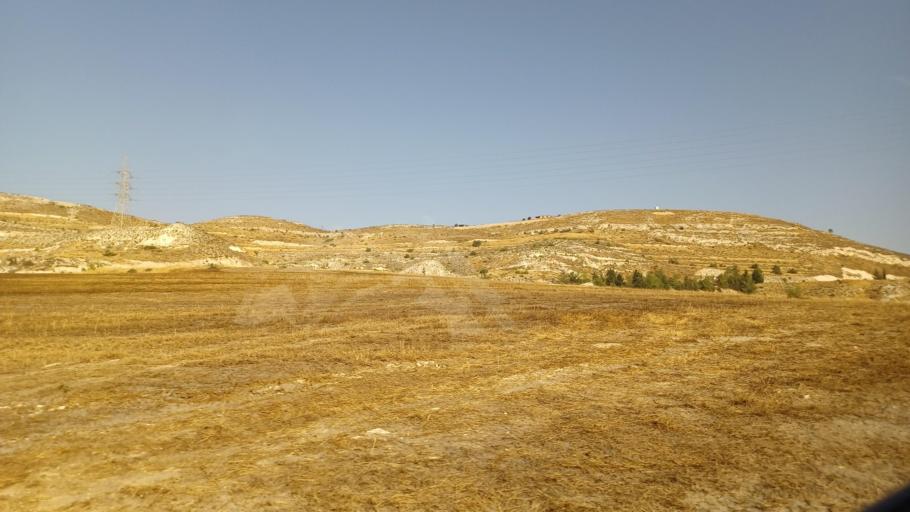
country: CY
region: Larnaka
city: Athienou
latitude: 35.0148
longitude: 33.5589
